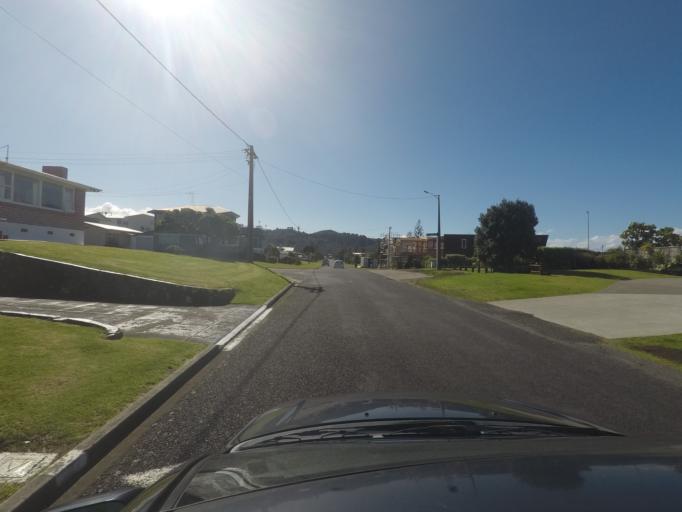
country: NZ
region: Bay of Plenty
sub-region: Western Bay of Plenty District
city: Waihi Beach
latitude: -37.4089
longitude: 175.9449
